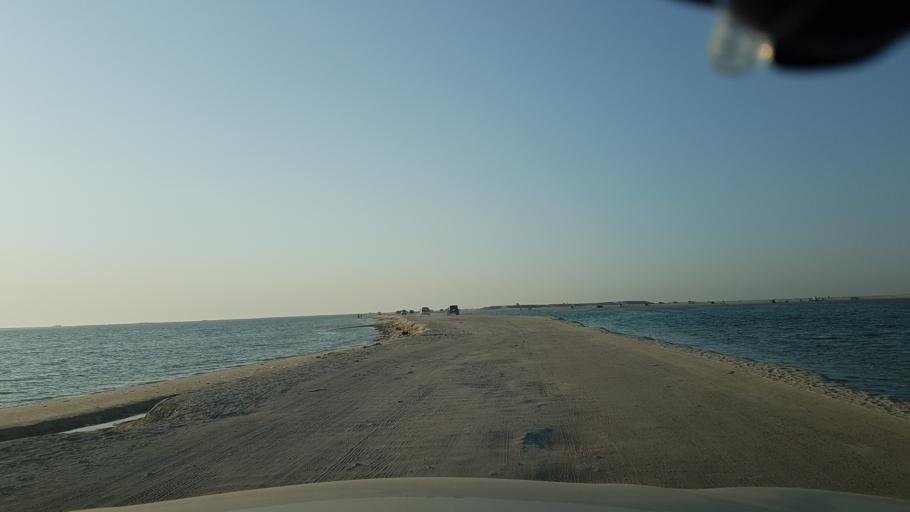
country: BH
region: Manama
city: Jidd Hafs
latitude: 26.2366
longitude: 50.5054
